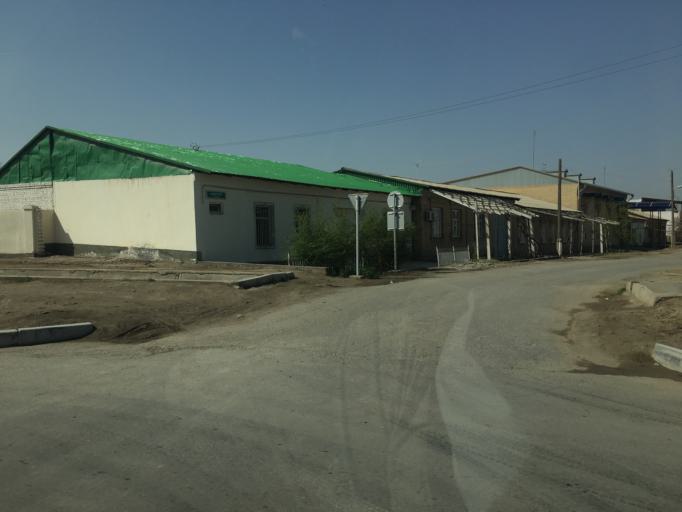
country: TM
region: Lebap
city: Turkmenabat
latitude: 39.0310
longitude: 63.5900
